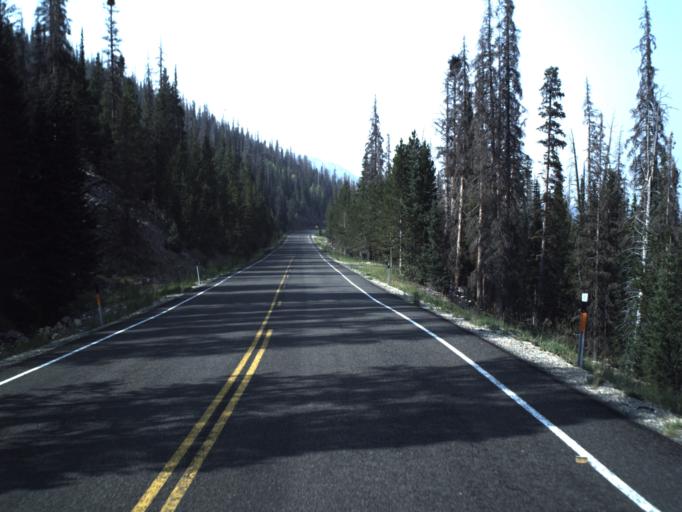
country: US
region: Utah
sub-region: Summit County
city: Kamas
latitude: 40.7687
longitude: -110.8831
